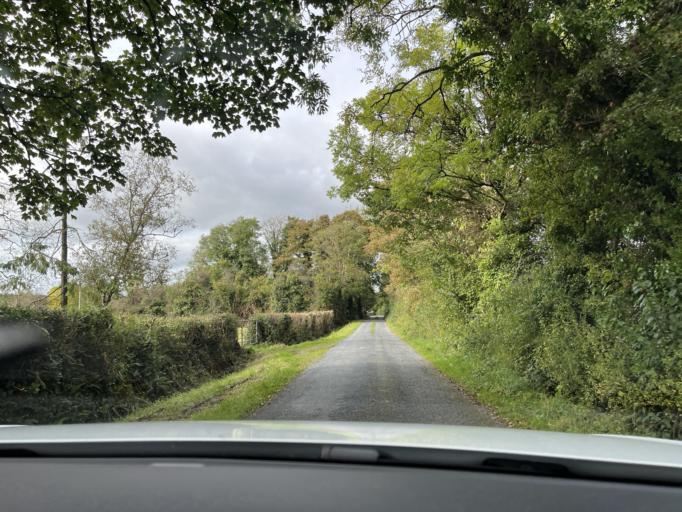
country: IE
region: Connaught
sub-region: County Leitrim
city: Carrick-on-Shannon
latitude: 53.9692
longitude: -8.0757
